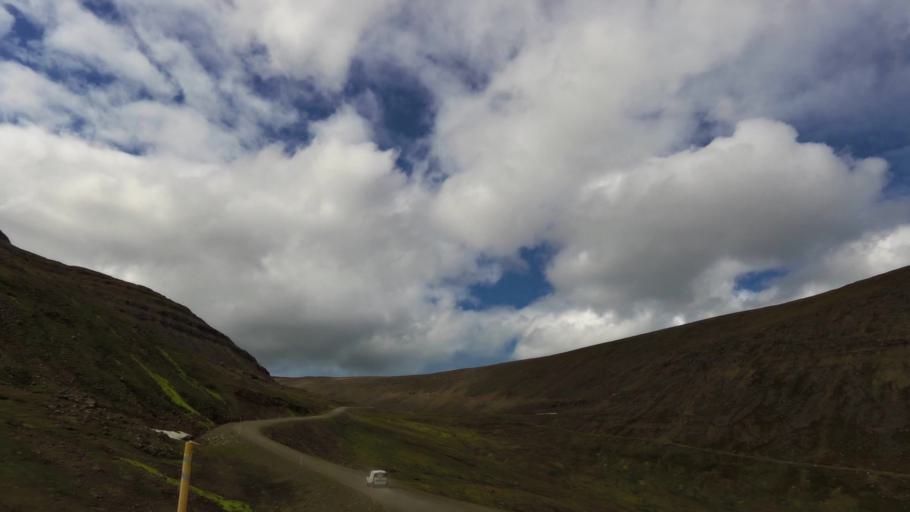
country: IS
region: Westfjords
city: Isafjoerdur
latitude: 66.1675
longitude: -23.3428
